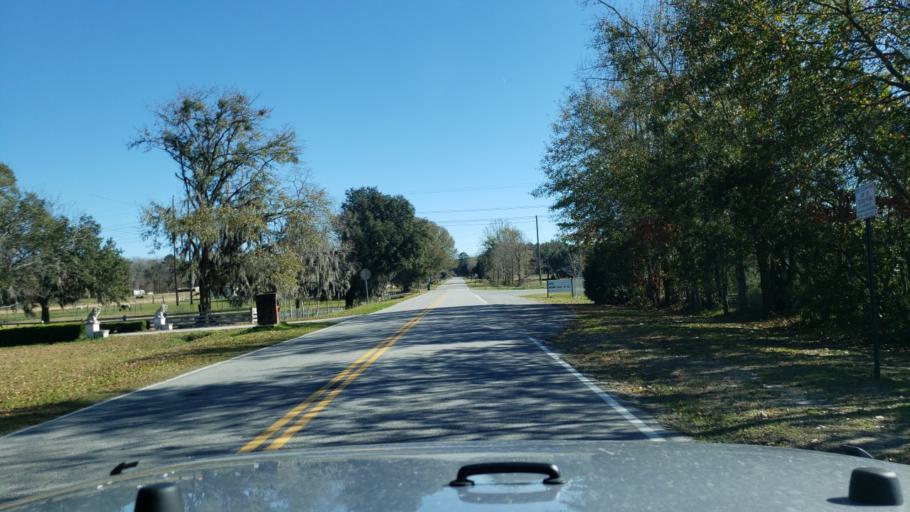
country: US
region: Georgia
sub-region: Chatham County
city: Georgetown
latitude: 32.0313
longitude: -81.1815
